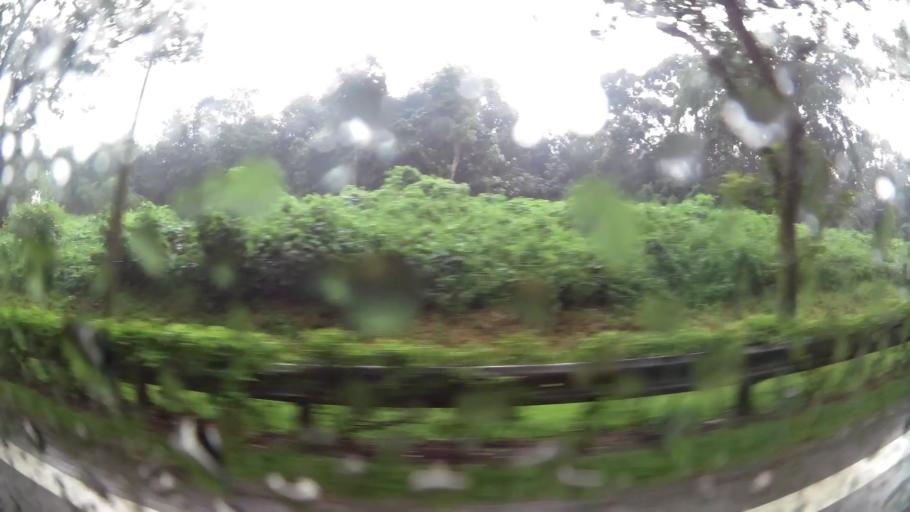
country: MY
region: Johor
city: Johor Bahru
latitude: 1.3934
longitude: 103.8210
